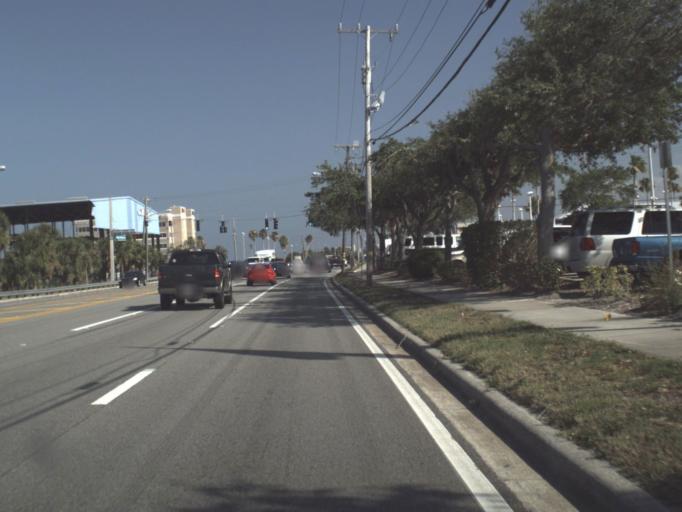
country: US
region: Florida
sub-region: Brevard County
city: Melbourne
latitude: 28.1008
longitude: -80.6135
